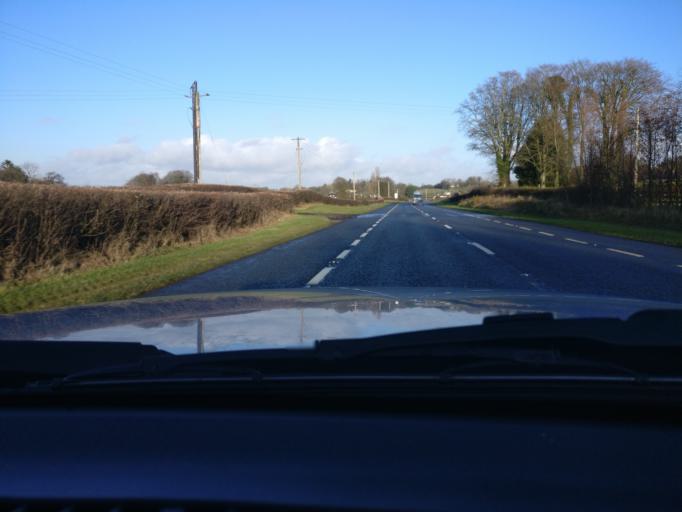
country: IE
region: Leinster
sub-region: An Iarmhi
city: An Muileann gCearr
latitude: 53.5405
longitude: -7.3020
